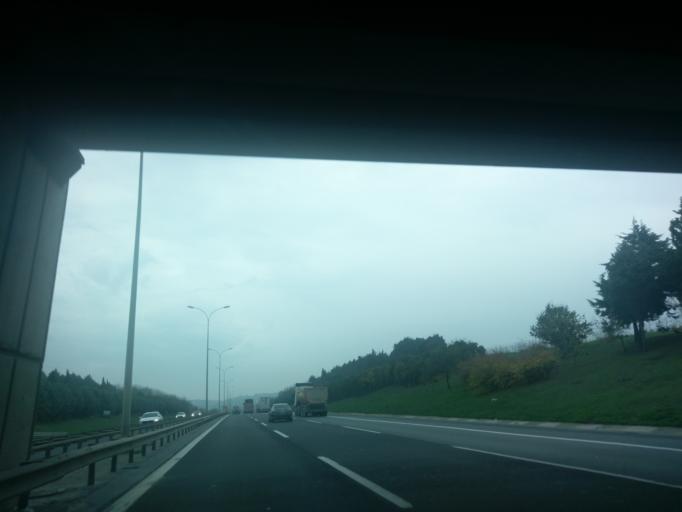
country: TR
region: Istanbul
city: Tepecik
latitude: 41.1052
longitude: 28.5846
